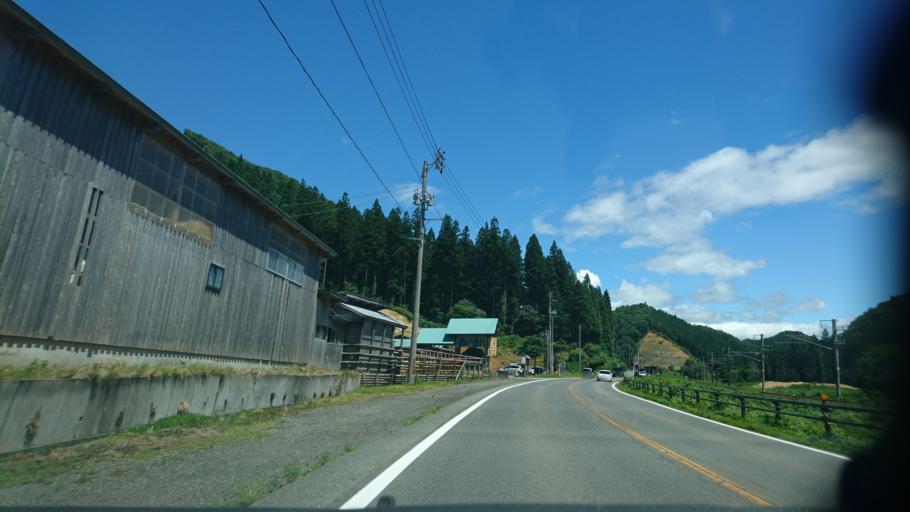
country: JP
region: Akita
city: Kakunodatemachi
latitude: 39.6471
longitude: 140.6647
